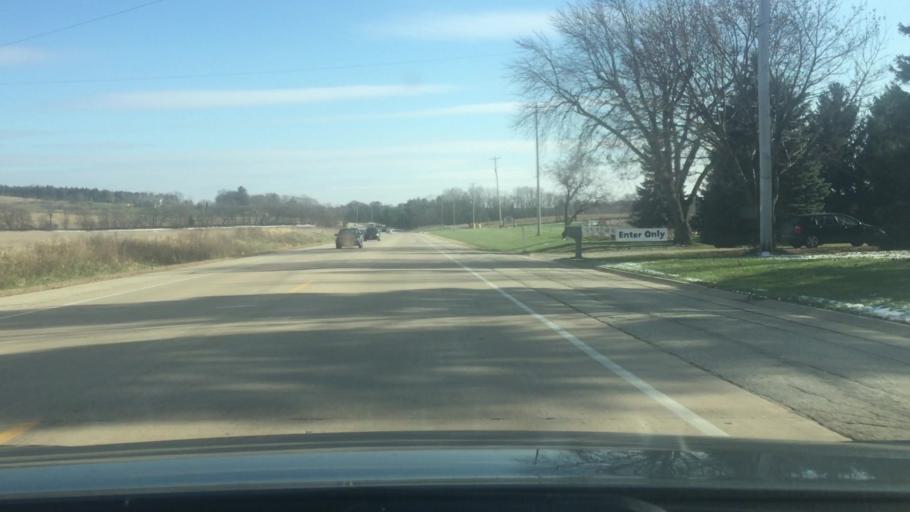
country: US
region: Wisconsin
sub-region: Jefferson County
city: Lake Koshkonong
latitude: 42.9689
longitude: -88.9131
